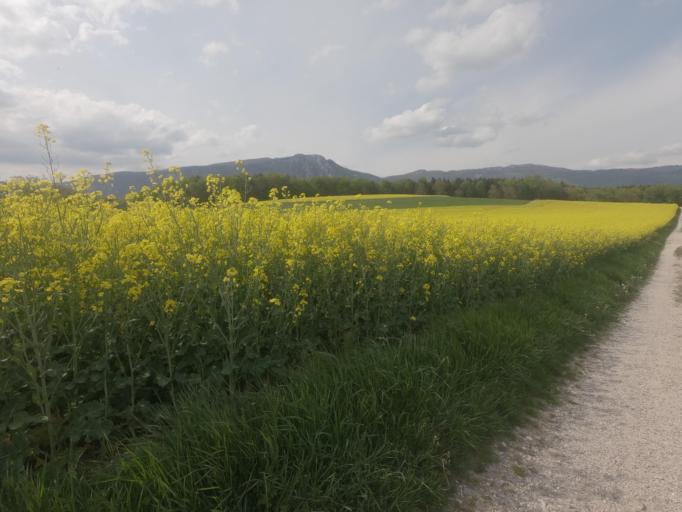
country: CH
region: Solothurn
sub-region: Bezirk Lebern
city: Riedholz
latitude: 47.2205
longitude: 7.5697
